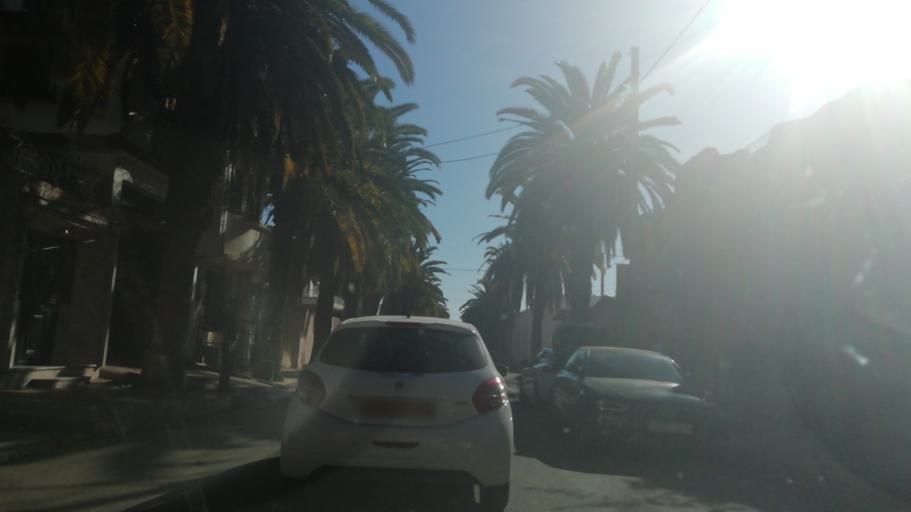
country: DZ
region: Oran
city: Oran
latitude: 35.6745
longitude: -0.6427
